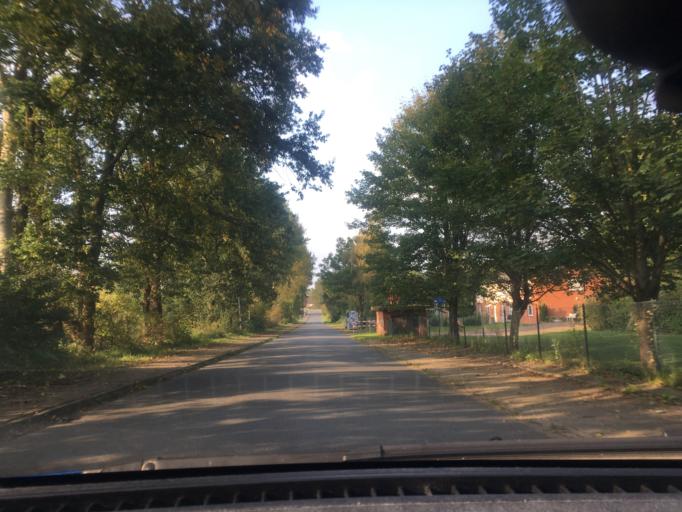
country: DE
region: Lower Saxony
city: Vastorf
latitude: 53.1924
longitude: 10.5493
